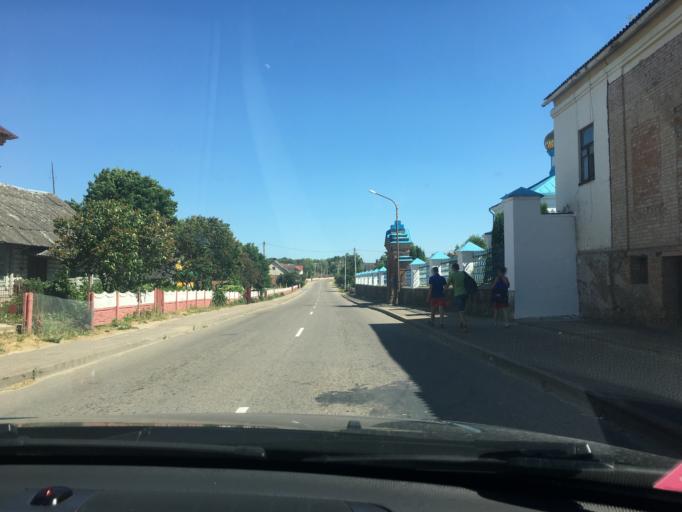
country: BY
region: Grodnenskaya
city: Hal'shany
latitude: 54.2562
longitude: 26.0128
